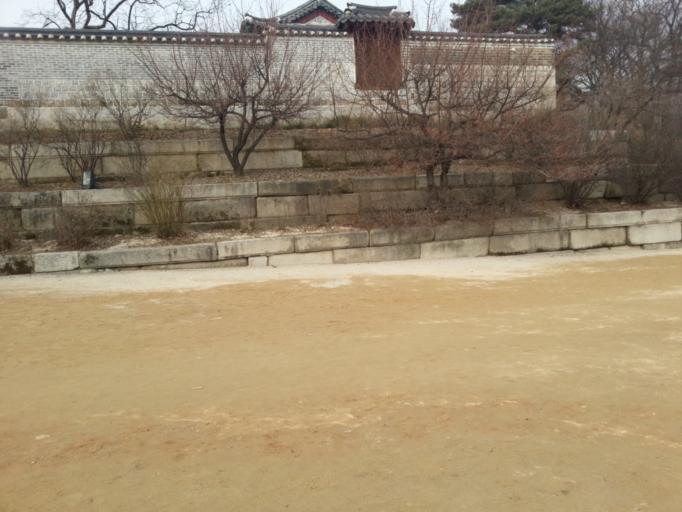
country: KR
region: Seoul
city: Seoul
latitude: 37.5787
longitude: 126.9943
